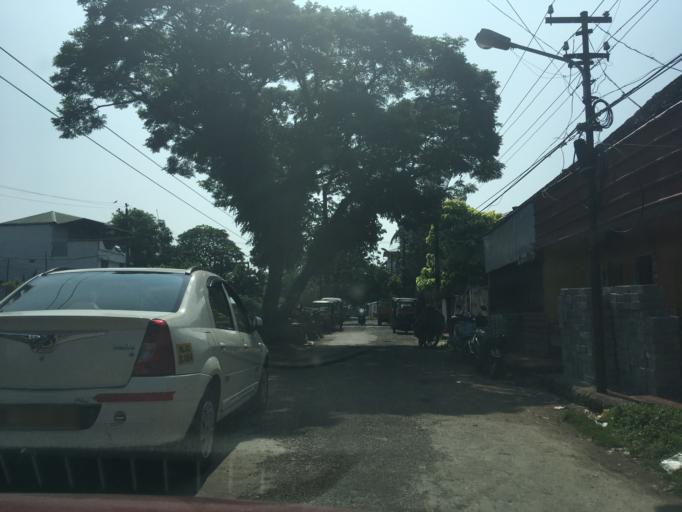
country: IN
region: Kerala
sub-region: Ernakulam
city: Cochin
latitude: 9.9666
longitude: 76.2505
